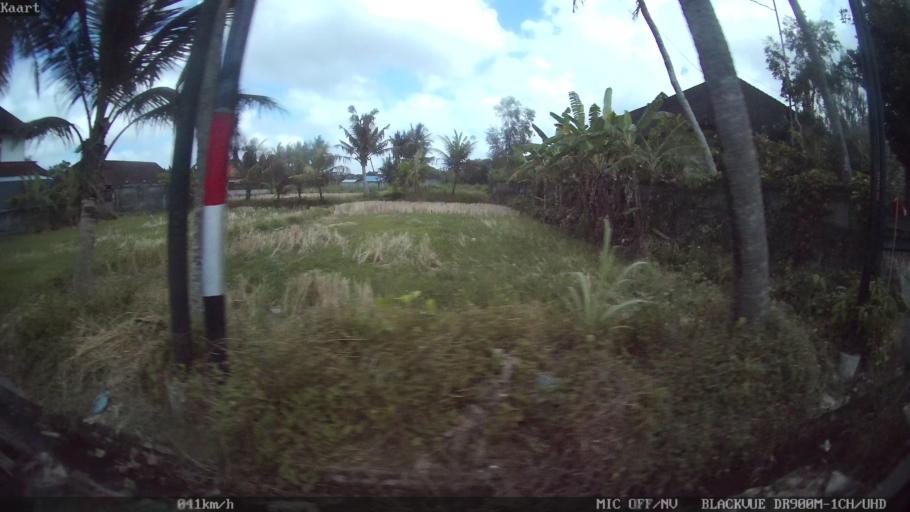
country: ID
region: Bali
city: Banjar Pasekan
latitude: -8.5819
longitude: 115.2951
